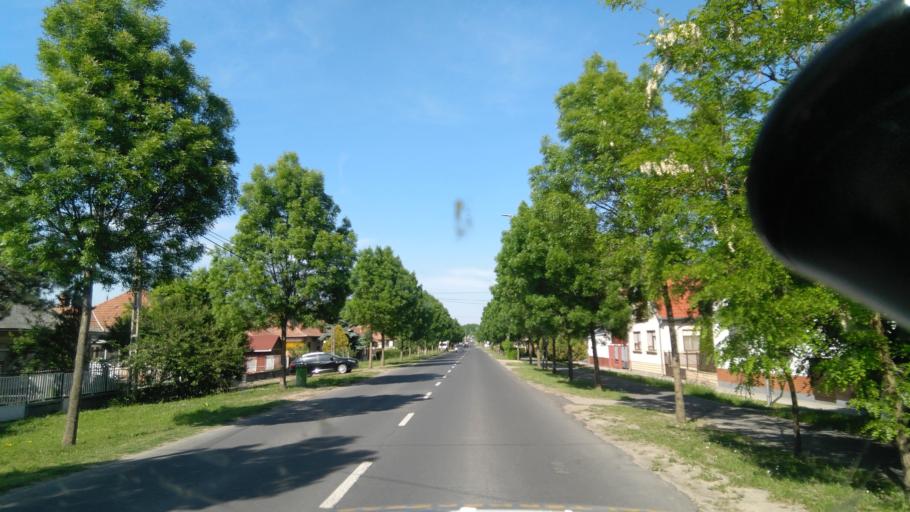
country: HU
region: Bekes
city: Gyula
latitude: 46.6608
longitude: 21.2912
